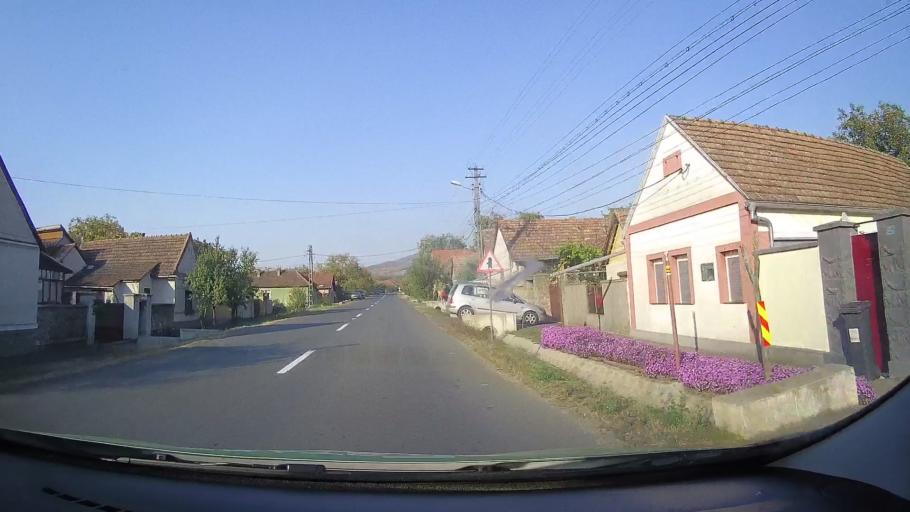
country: RO
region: Arad
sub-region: Comuna Paulis
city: Paulis
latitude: 46.1331
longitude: 21.6026
